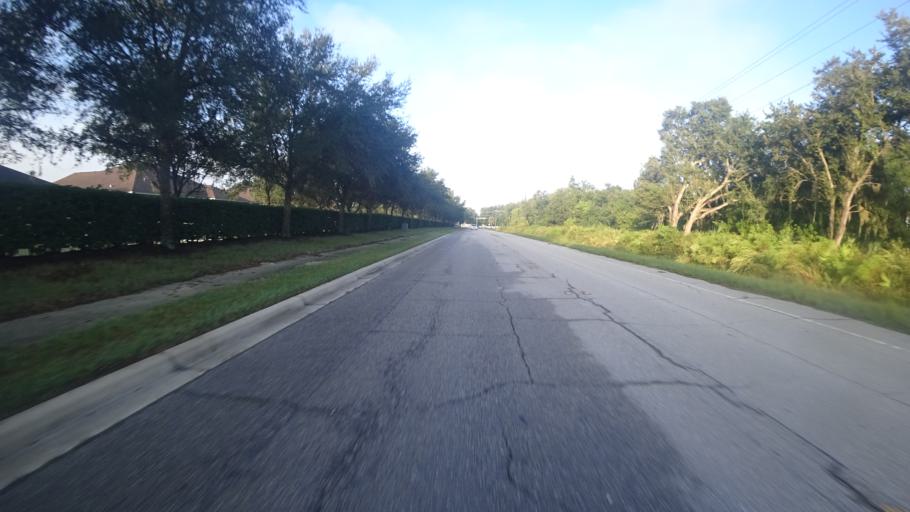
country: US
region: Florida
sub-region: Manatee County
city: Ellenton
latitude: 27.5353
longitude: -82.4235
